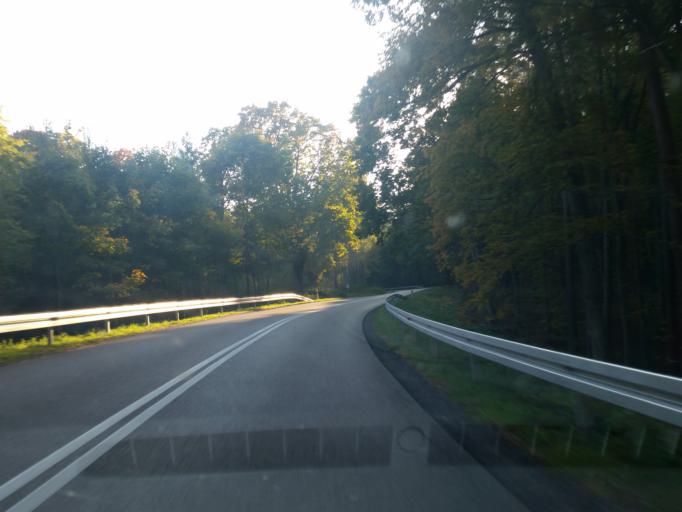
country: PL
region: Kujawsko-Pomorskie
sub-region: Powiat brodnicki
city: Gorzno
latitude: 53.2483
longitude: 19.7071
